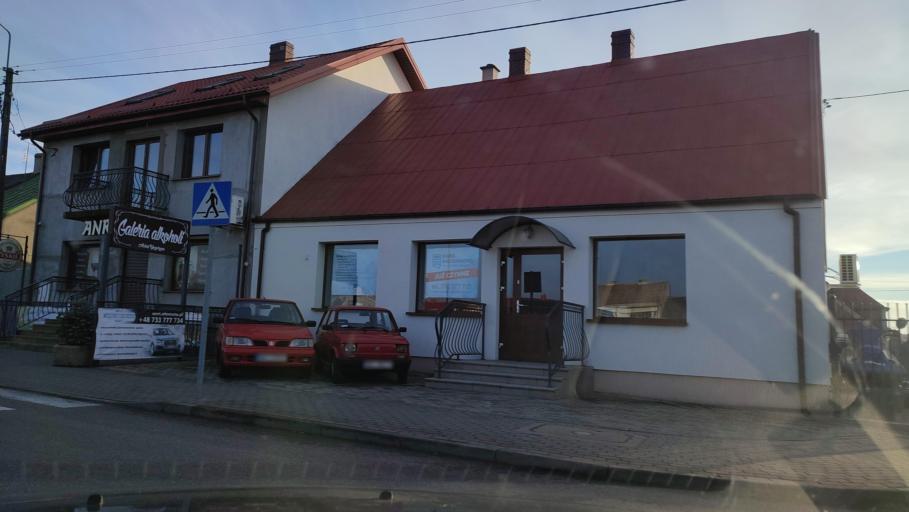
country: PL
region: Masovian Voivodeship
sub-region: Powiat mlawski
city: Dzierzgowo
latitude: 53.3173
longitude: 20.6696
